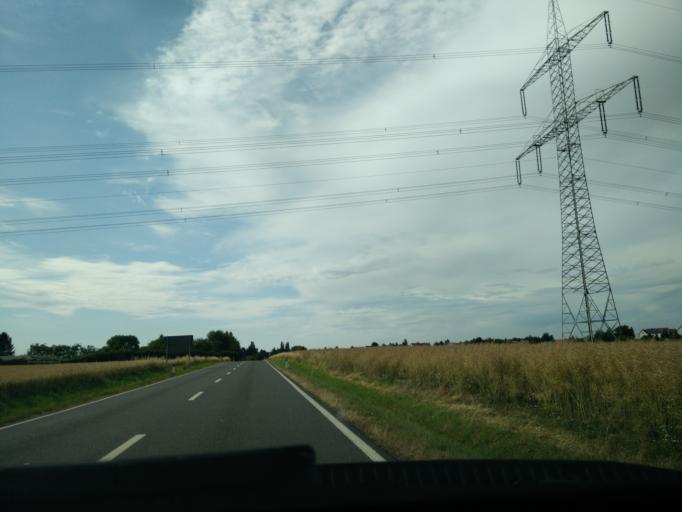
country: DE
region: Saxony
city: Geithain
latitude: 51.0832
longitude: 12.6478
